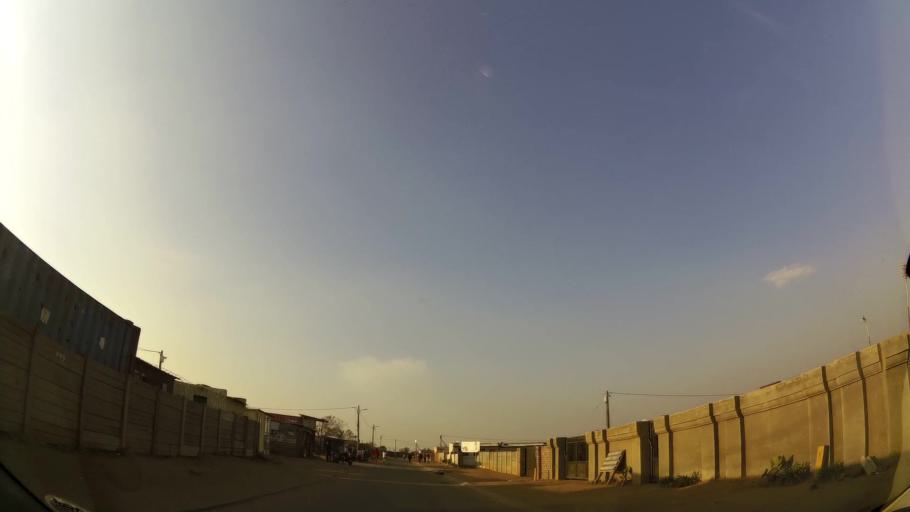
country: ZA
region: Gauteng
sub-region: Ekurhuleni Metropolitan Municipality
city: Benoni
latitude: -26.1557
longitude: 28.3800
